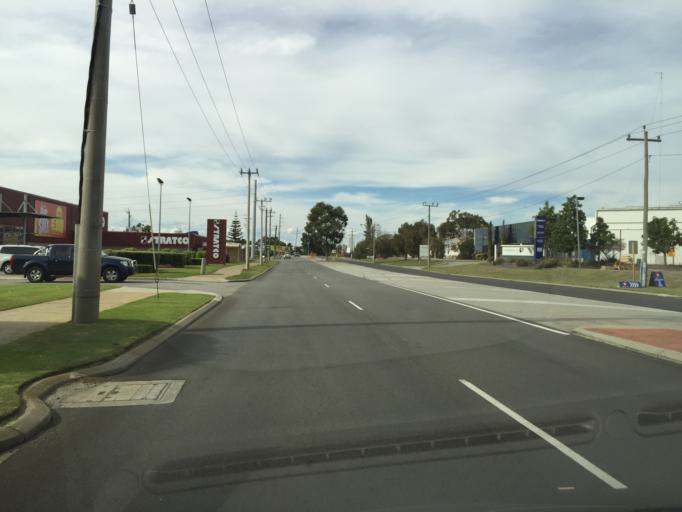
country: AU
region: Western Australia
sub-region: Canning
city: Canning Vale
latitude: -32.0624
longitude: 115.9043
